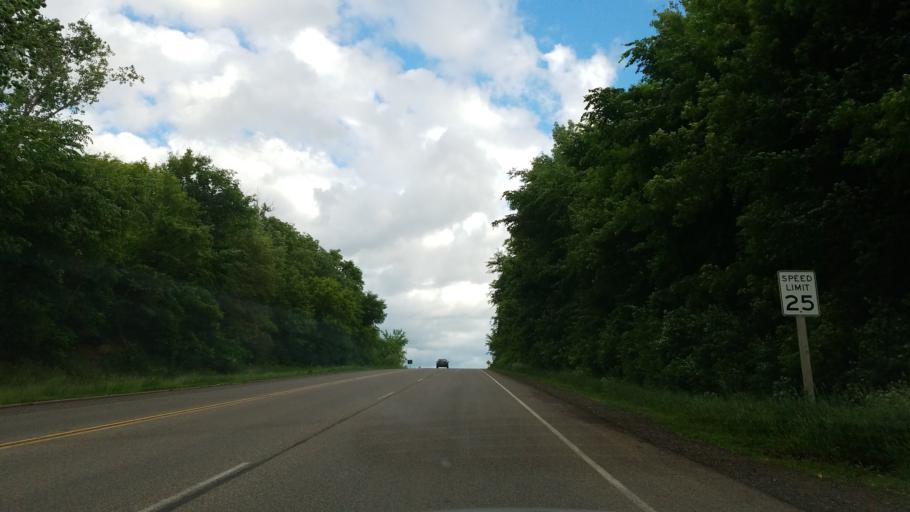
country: US
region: Wisconsin
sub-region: Polk County
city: Osceola
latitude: 45.3173
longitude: -92.7047
